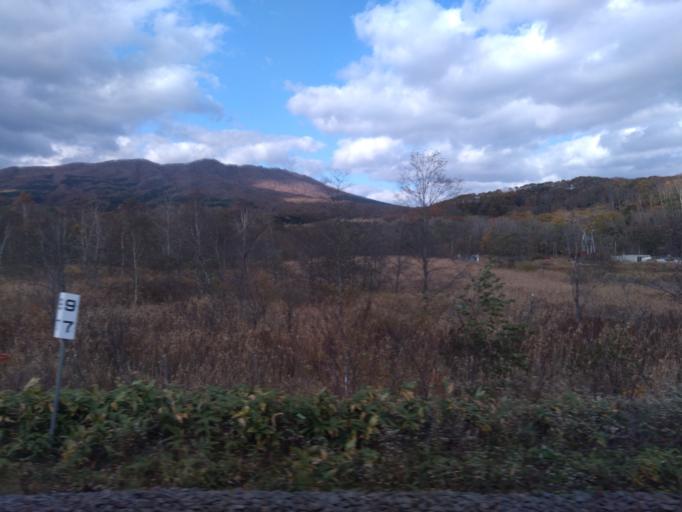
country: JP
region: Hokkaido
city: Shiraoi
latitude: 42.4614
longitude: 141.2037
